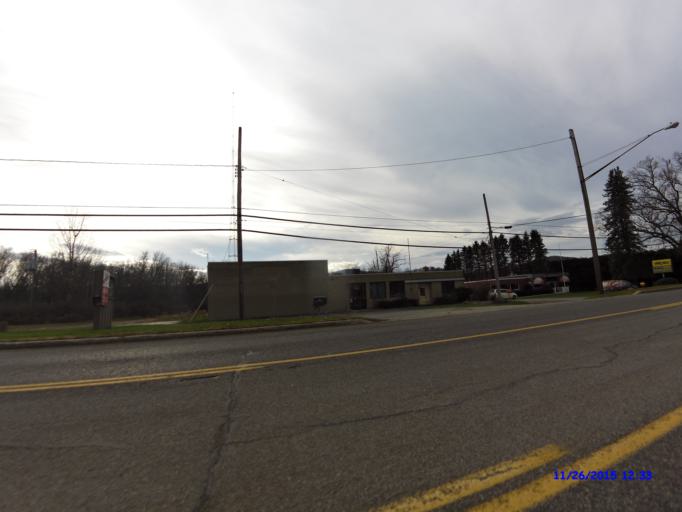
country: US
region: New York
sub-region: Cattaraugus County
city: Saint Bonaventure
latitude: 42.0773
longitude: -78.4729
